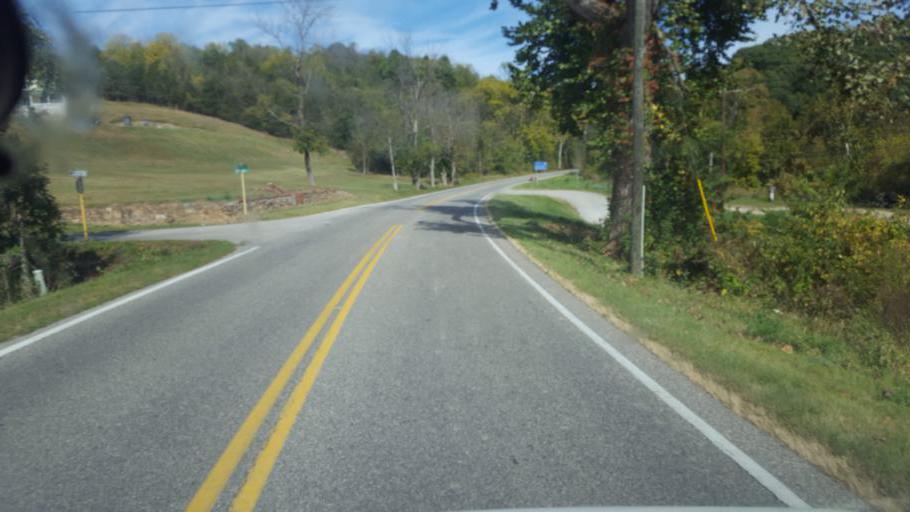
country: US
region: Virginia
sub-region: Page County
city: Stanley
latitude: 38.5827
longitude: -78.5957
